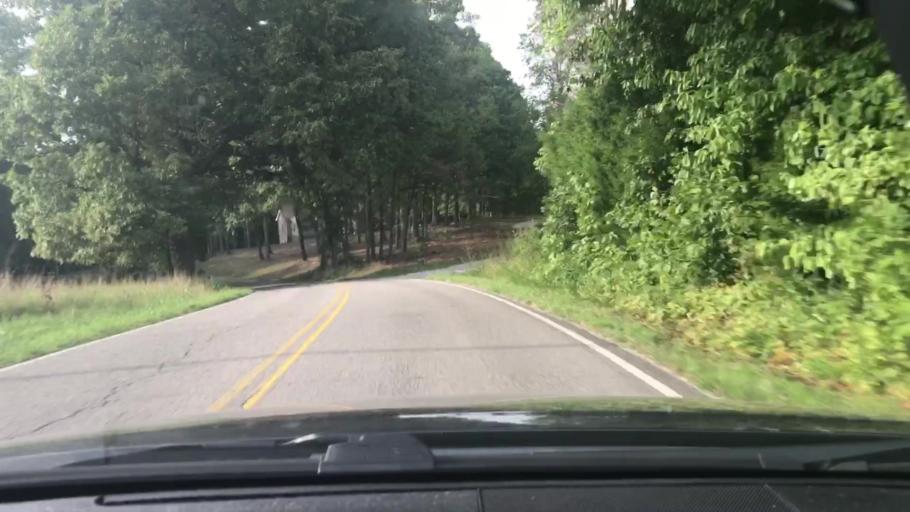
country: US
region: Tennessee
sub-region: Dickson County
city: White Bluff
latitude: 36.1688
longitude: -87.2622
